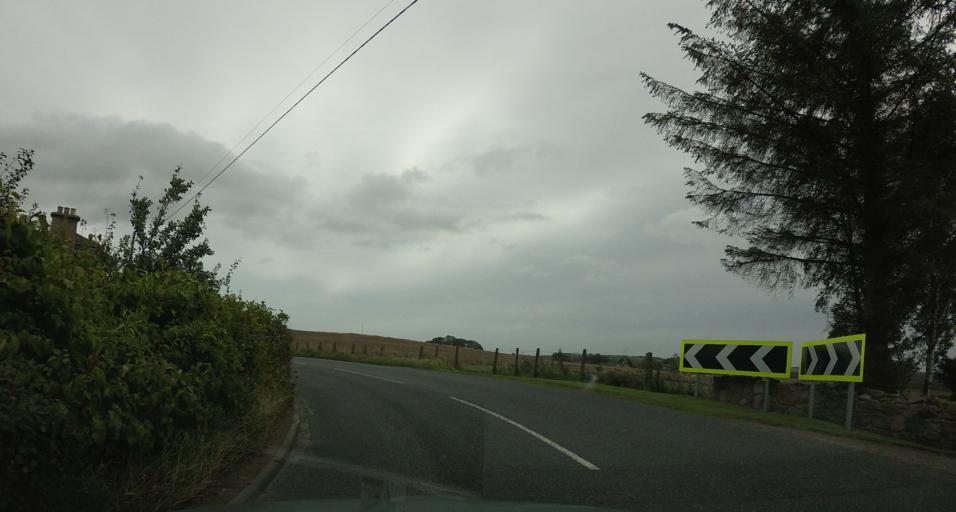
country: GB
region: Scotland
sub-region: Aberdeenshire
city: Kemnay
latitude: 57.2209
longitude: -2.4704
